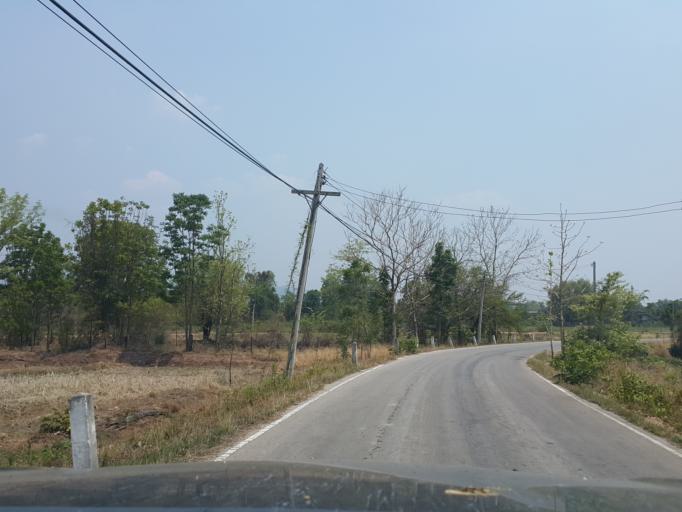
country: TH
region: Lampang
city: Mae Phrik
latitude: 17.5184
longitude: 99.1472
